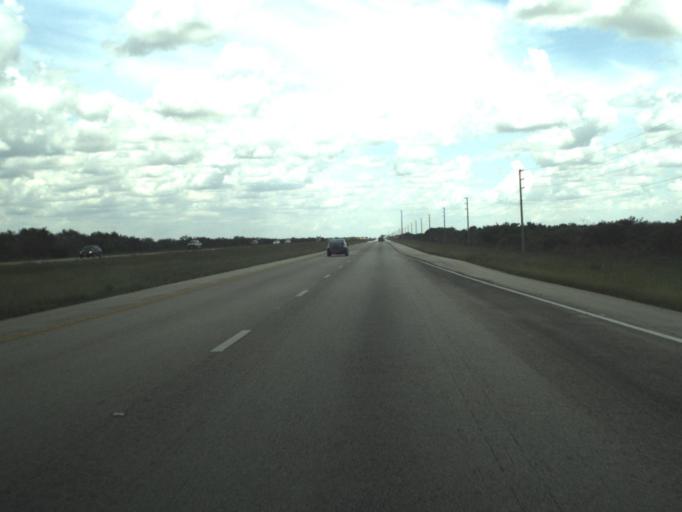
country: US
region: Florida
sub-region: Broward County
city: Weston
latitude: 26.1655
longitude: -80.8236
